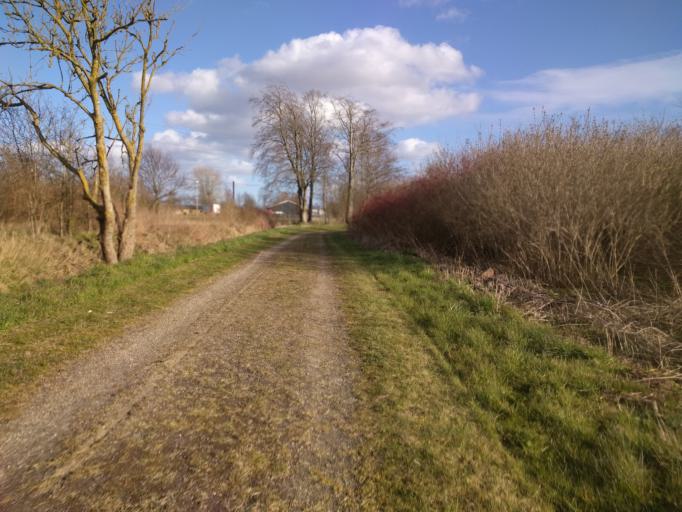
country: DK
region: South Denmark
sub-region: Odense Kommune
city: Neder Holluf
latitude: 55.3702
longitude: 10.5024
